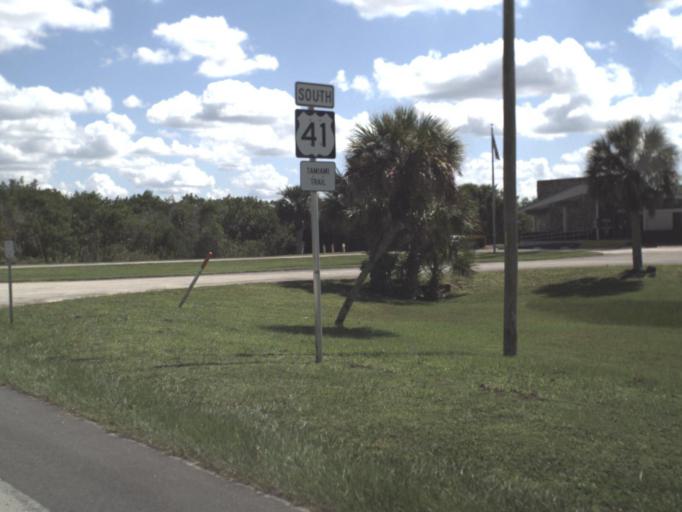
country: US
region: Florida
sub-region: Collier County
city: Marco
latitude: 25.9107
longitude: -81.3642
